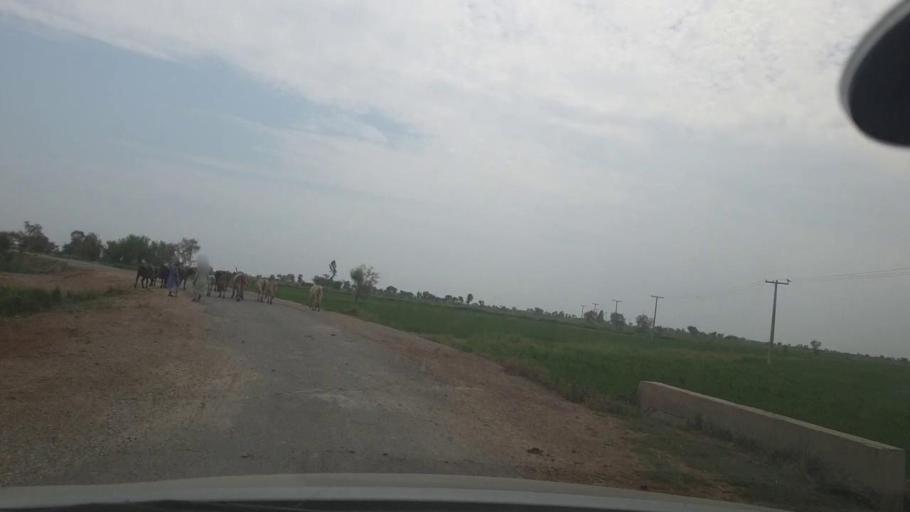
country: PK
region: Balochistan
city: Garhi Khairo
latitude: 28.0243
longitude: 68.0428
